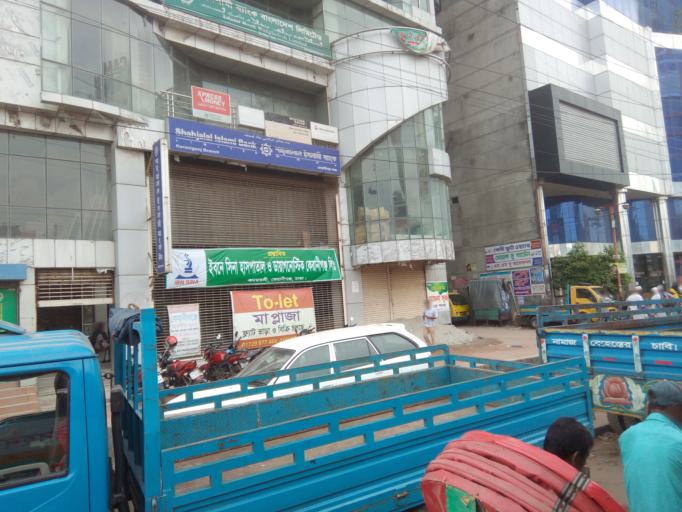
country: BD
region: Dhaka
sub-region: Dhaka
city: Dhaka
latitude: 23.7027
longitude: 90.3976
